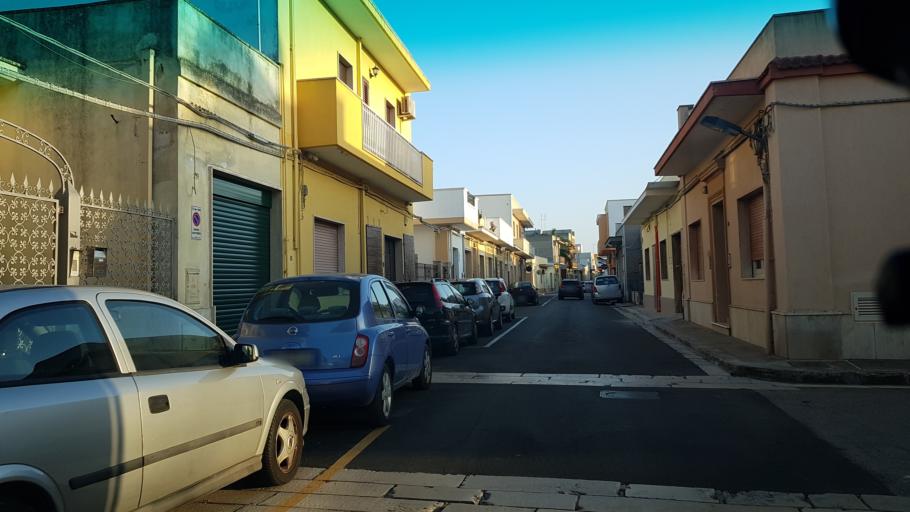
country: IT
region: Apulia
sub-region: Provincia di Brindisi
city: Mesagne
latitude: 40.5548
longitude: 17.8032
